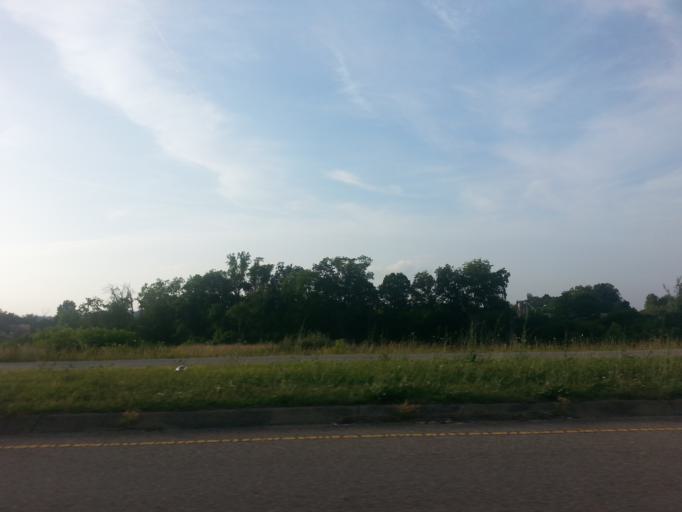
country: US
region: Tennessee
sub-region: Knox County
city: Farragut
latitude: 35.9564
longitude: -84.1377
